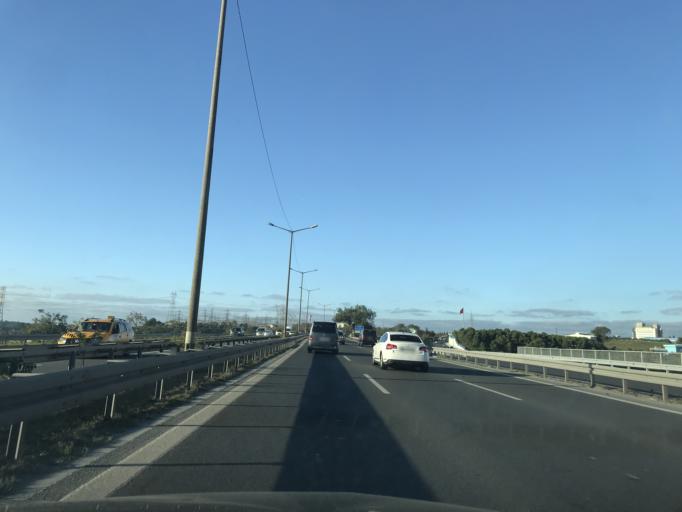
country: TR
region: Istanbul
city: Sisli
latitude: 41.0867
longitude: 28.9610
